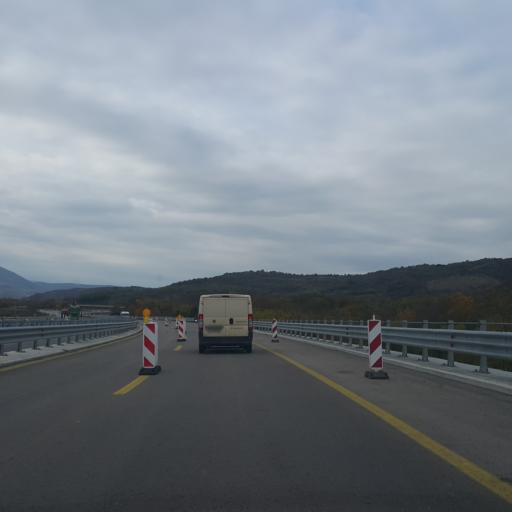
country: RS
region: Central Serbia
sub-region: Pirotski Okrug
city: Bela Palanka
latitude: 43.2346
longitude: 22.3746
